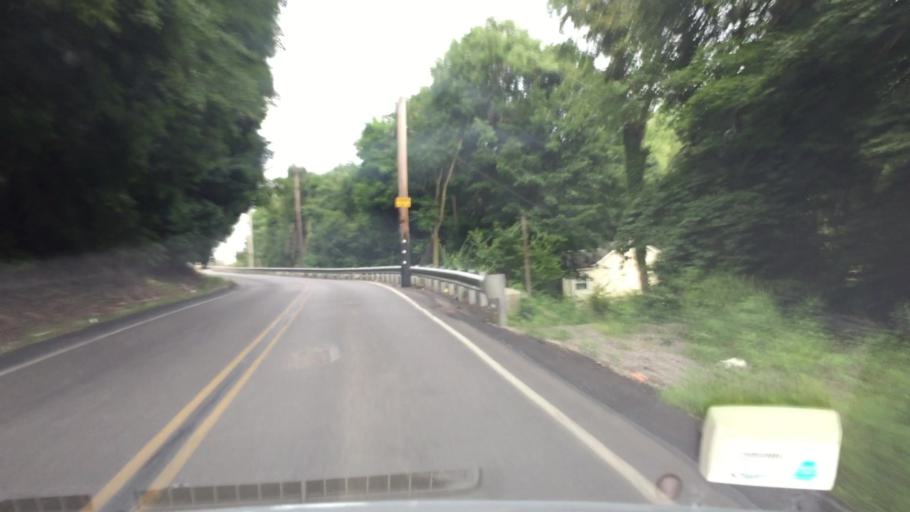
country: US
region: Pennsylvania
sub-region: Allegheny County
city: McKees Rocks
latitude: 40.4760
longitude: -80.0681
